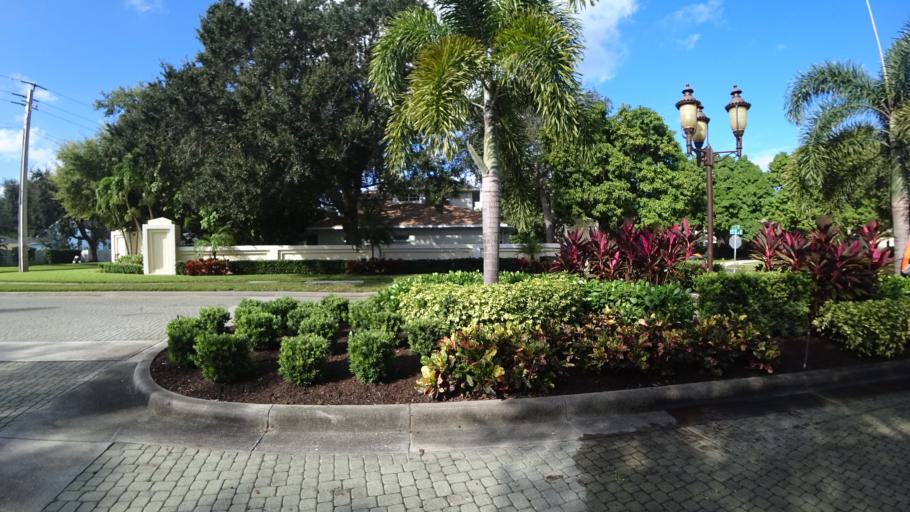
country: US
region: Florida
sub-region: Manatee County
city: West Bradenton
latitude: 27.5149
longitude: -82.6533
